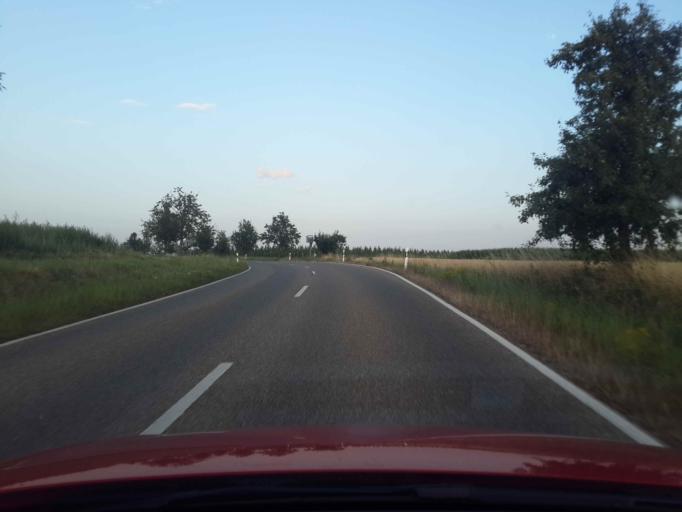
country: DE
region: Baden-Wuerttemberg
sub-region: Regierungsbezirk Stuttgart
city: Brackenheim
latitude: 49.0802
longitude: 9.0485
